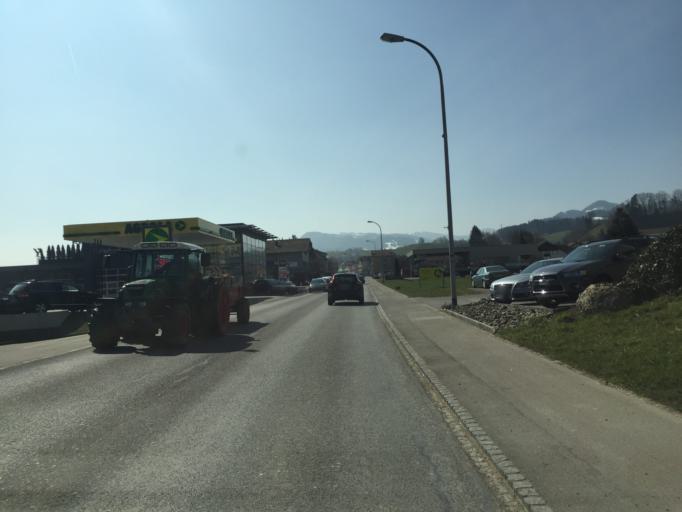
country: CH
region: Saint Gallen
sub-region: Wahlkreis Toggenburg
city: Buetschwil
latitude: 47.3672
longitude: 9.0755
